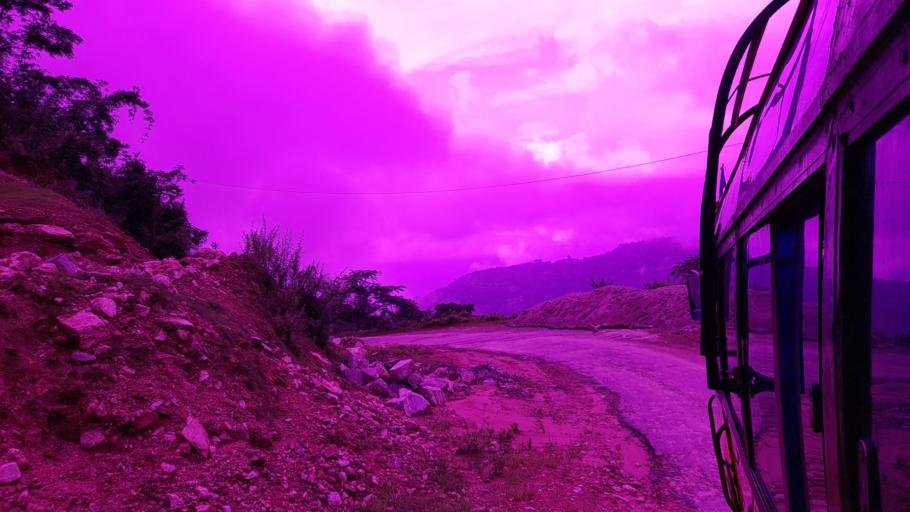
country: NP
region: Central Region
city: Kirtipur
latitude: 27.8219
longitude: 85.2102
